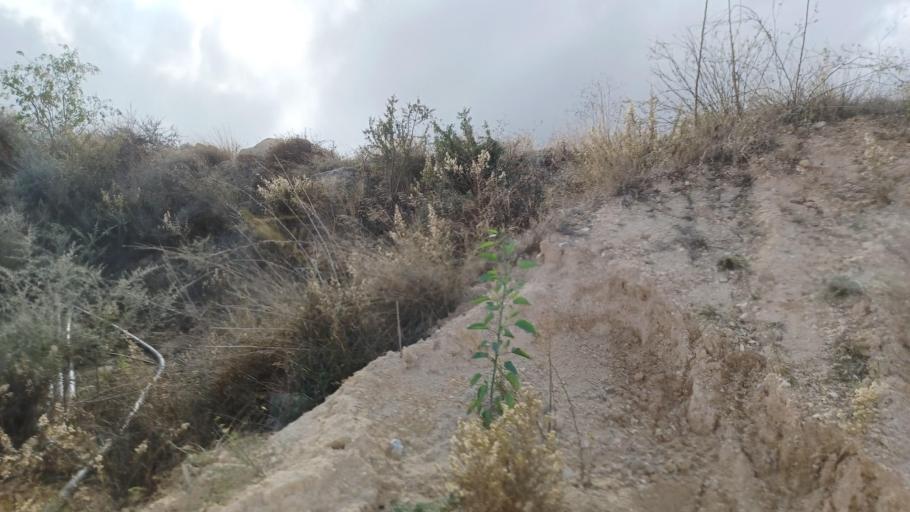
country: CY
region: Pafos
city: Polis
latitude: 35.0002
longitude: 32.3927
